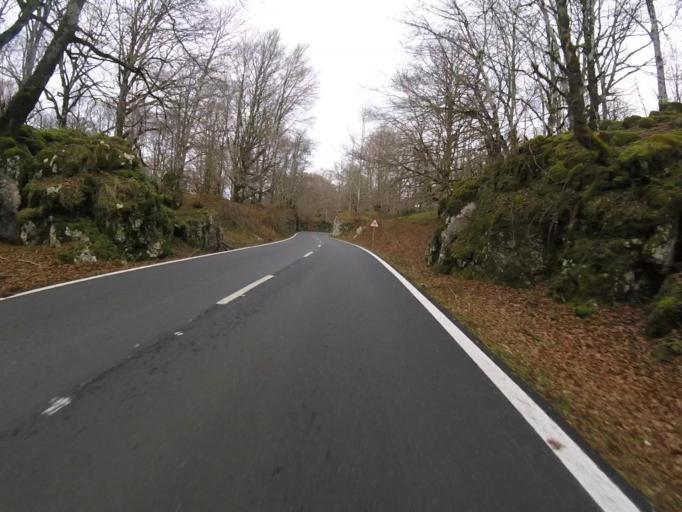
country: ES
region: Navarre
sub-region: Provincia de Navarra
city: Olazagutia
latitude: 42.8442
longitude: -2.1792
